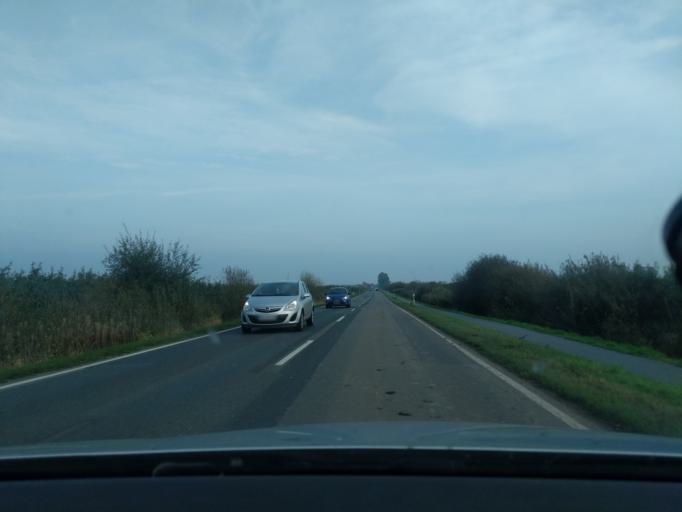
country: DE
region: Lower Saxony
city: Guderhandviertel
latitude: 53.5451
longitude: 9.5913
